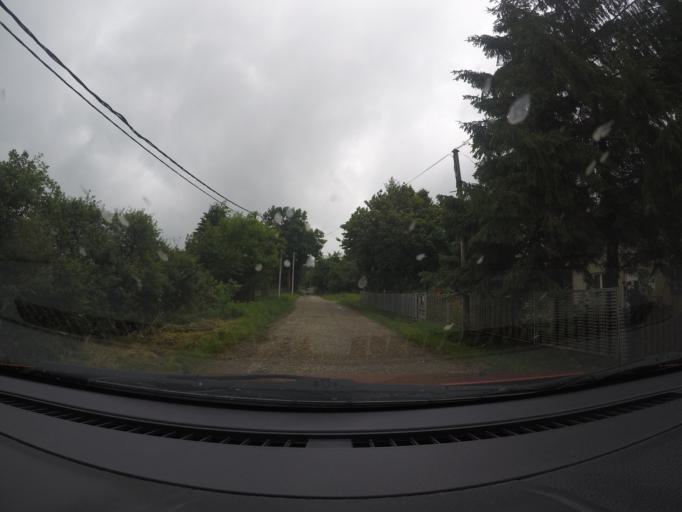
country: RS
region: Central Serbia
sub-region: Belgrade
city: Sopot
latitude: 44.5545
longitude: 20.5158
